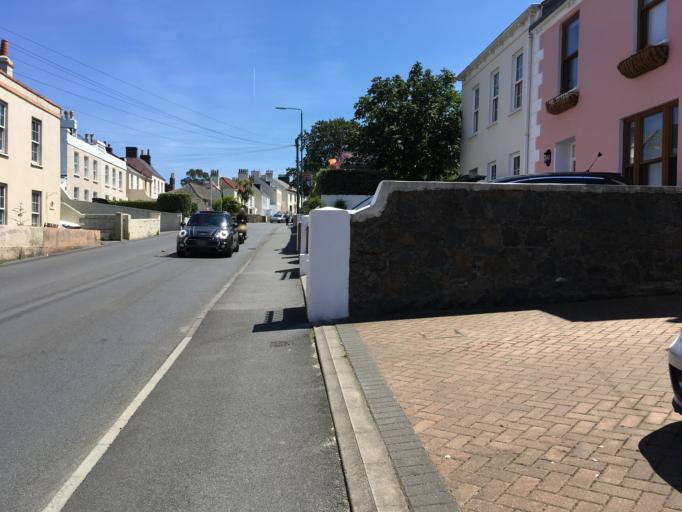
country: GG
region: St Peter Port
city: Saint Peter Port
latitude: 49.4598
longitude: -2.5571
